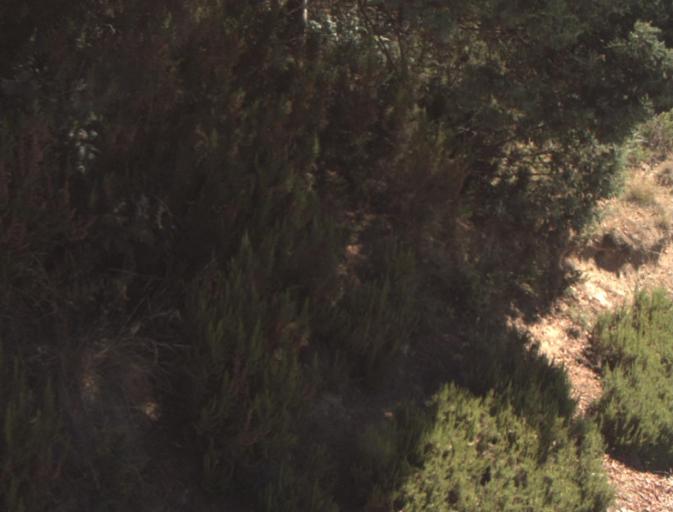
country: AU
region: Tasmania
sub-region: Dorset
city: Scottsdale
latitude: -41.3043
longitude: 147.3675
